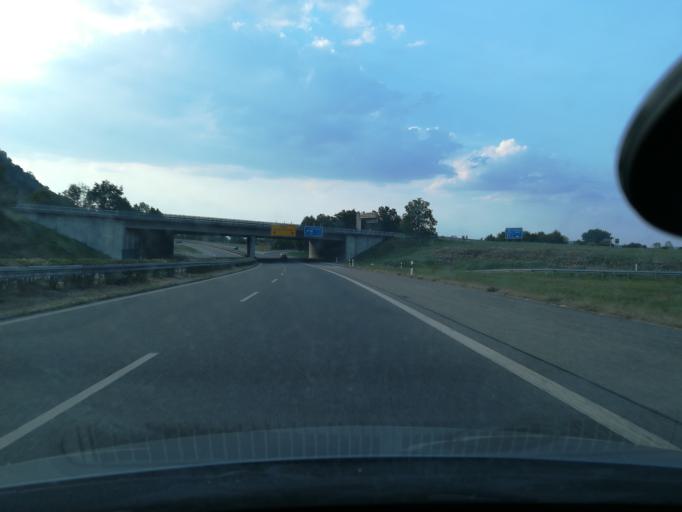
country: DE
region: Baden-Wuerttemberg
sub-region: Freiburg Region
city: Muhlhausen-Ehingen
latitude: 47.7921
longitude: 8.8302
